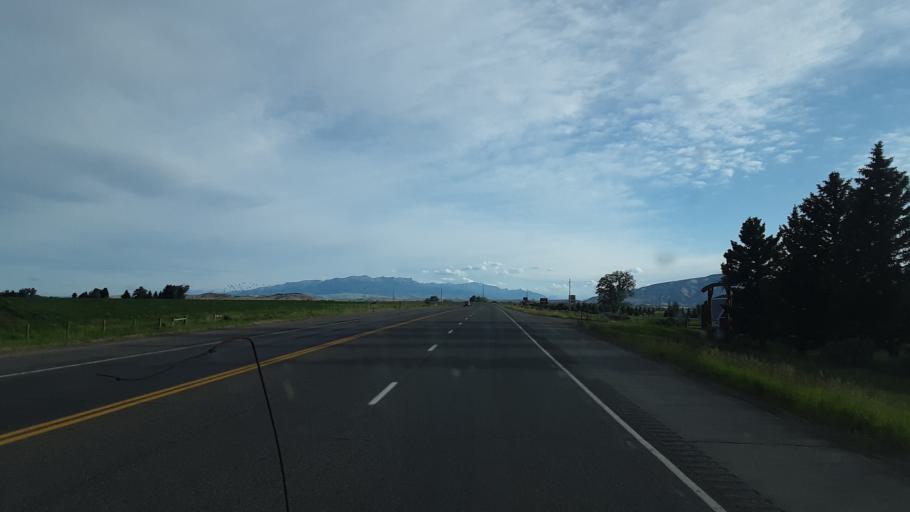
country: US
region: Wyoming
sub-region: Park County
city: Cody
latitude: 44.5720
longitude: -108.9762
